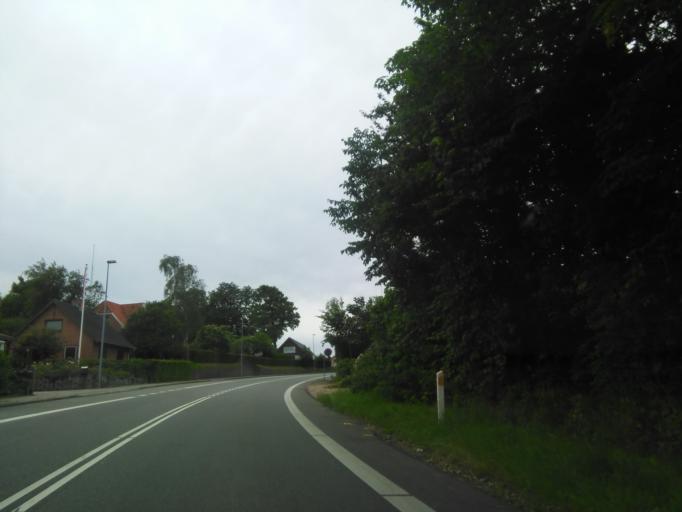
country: DK
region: Central Jutland
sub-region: Skanderborg Kommune
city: Stilling
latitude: 55.9892
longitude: 10.0232
